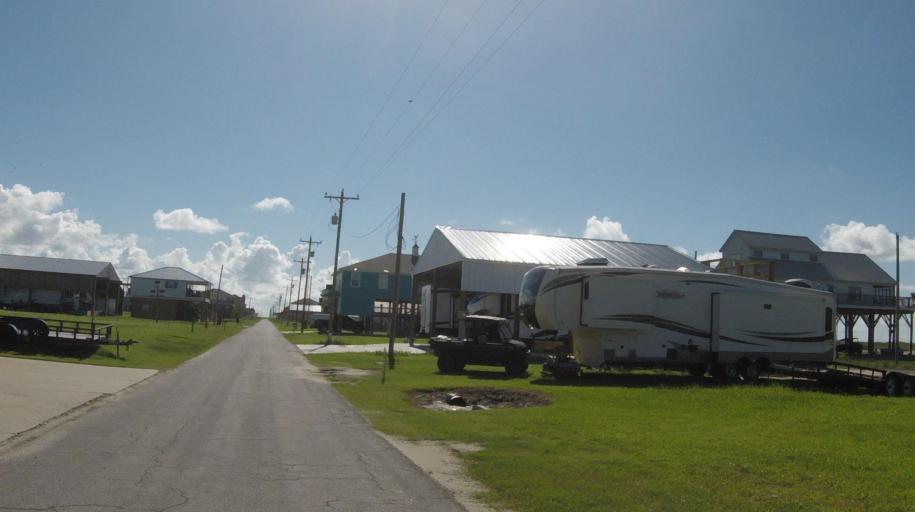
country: US
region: Louisiana
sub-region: Cameron Parish
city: Cameron
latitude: 29.7706
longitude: -93.4560
